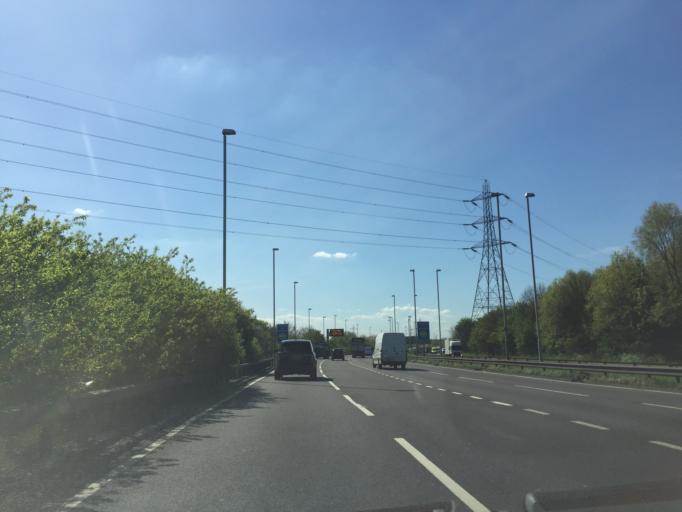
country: GB
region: England
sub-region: Greater London
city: Woodford Green
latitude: 51.5880
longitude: 0.0400
